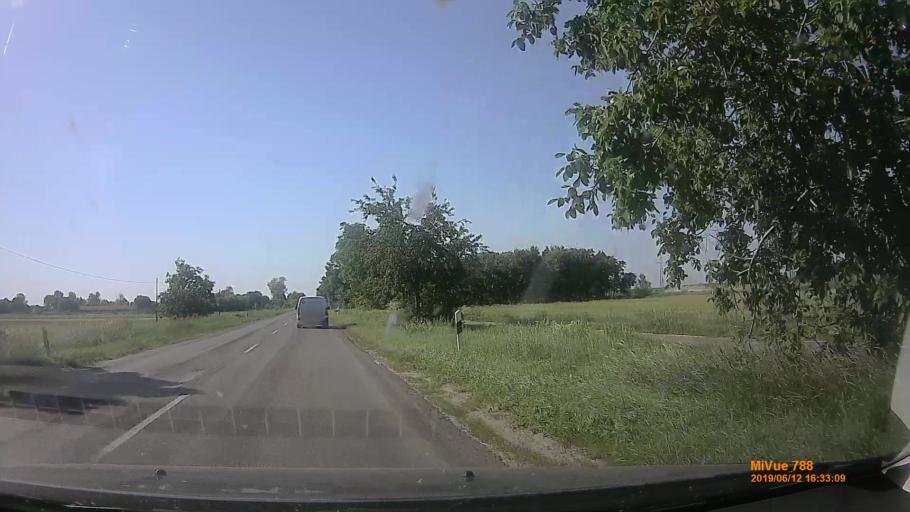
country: HU
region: Csongrad
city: Apatfalva
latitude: 46.1843
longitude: 20.5682
